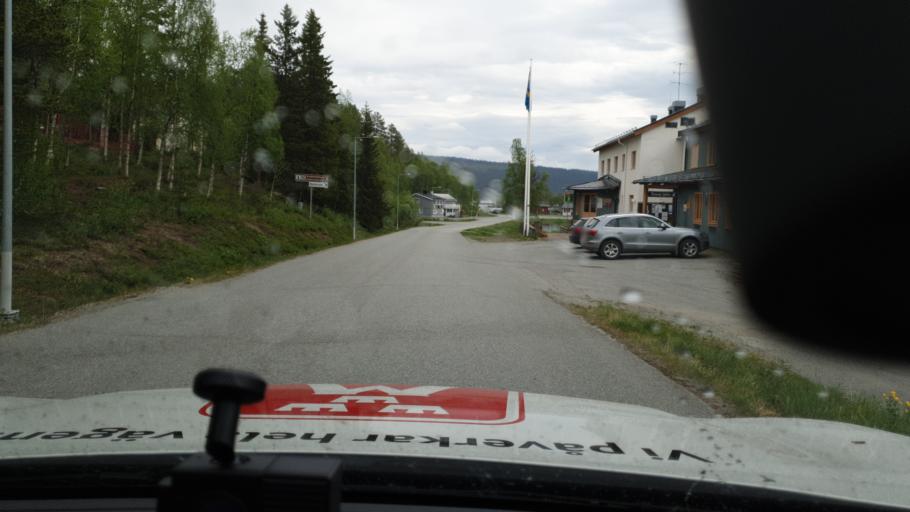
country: SE
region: Vaesterbotten
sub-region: Storumans Kommun
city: Fristad
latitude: 65.9574
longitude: 16.2048
